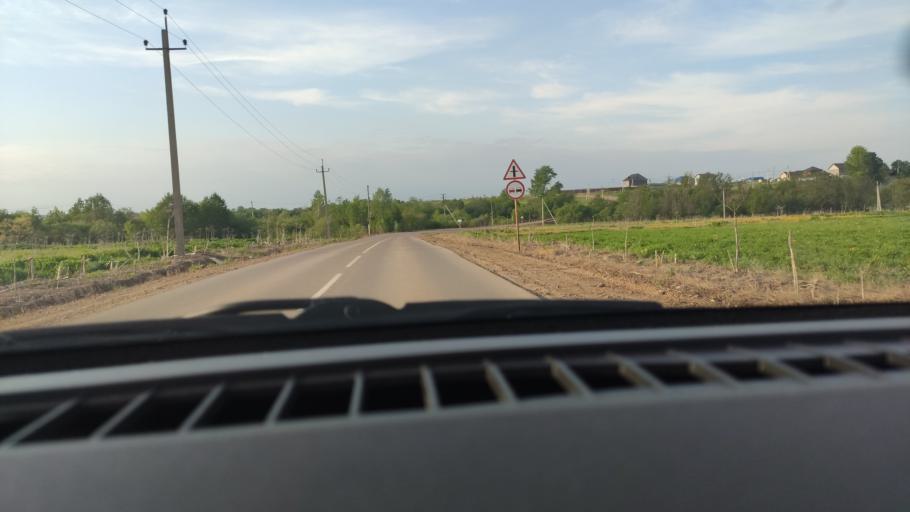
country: RU
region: Perm
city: Kultayevo
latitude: 57.8948
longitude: 55.9915
